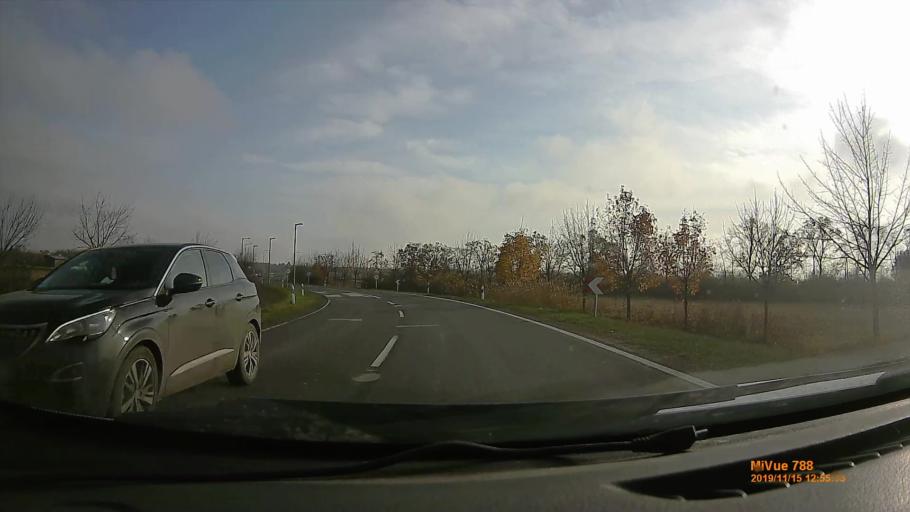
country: HU
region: Bekes
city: Bekescsaba
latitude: 46.6783
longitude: 21.1286
